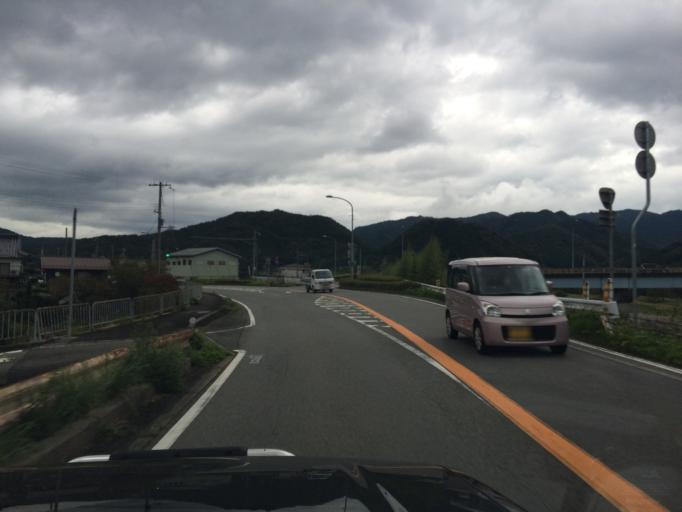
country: JP
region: Hyogo
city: Toyooka
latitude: 35.4193
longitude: 134.7898
